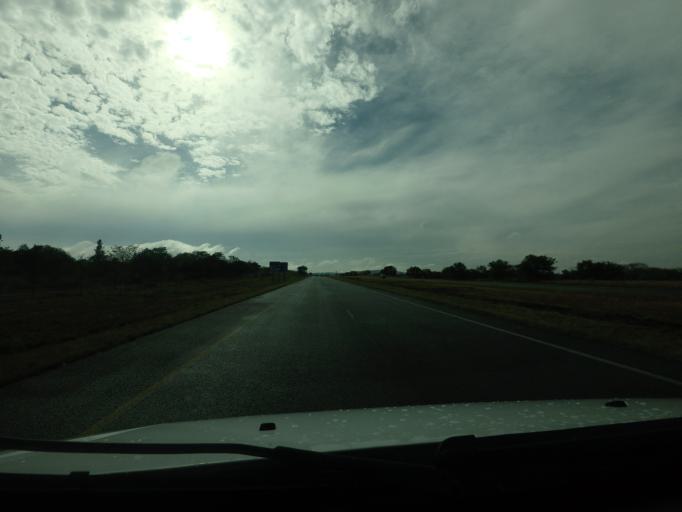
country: ZA
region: Gauteng
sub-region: City of Tshwane Metropolitan Municipality
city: Cullinan
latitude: -25.7717
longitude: 28.4241
